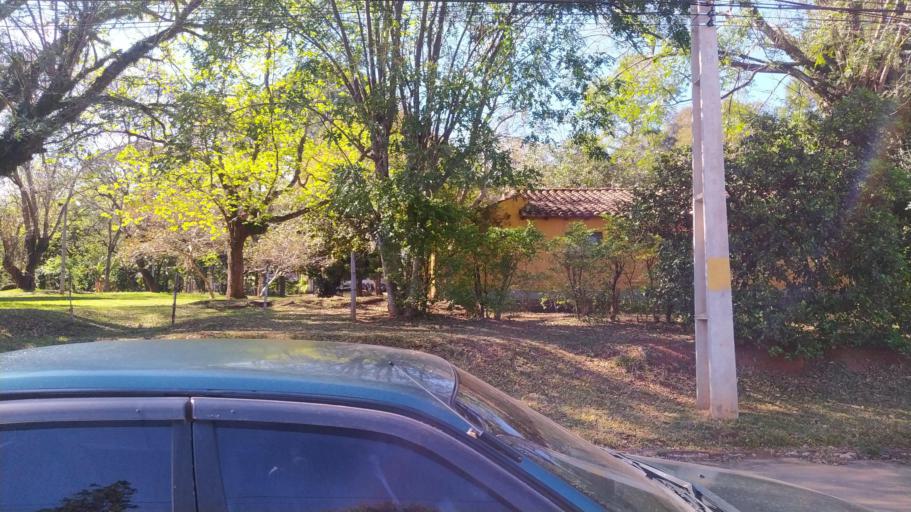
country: PY
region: Misiones
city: San Juan Bautista
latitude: -26.6690
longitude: -57.1363
